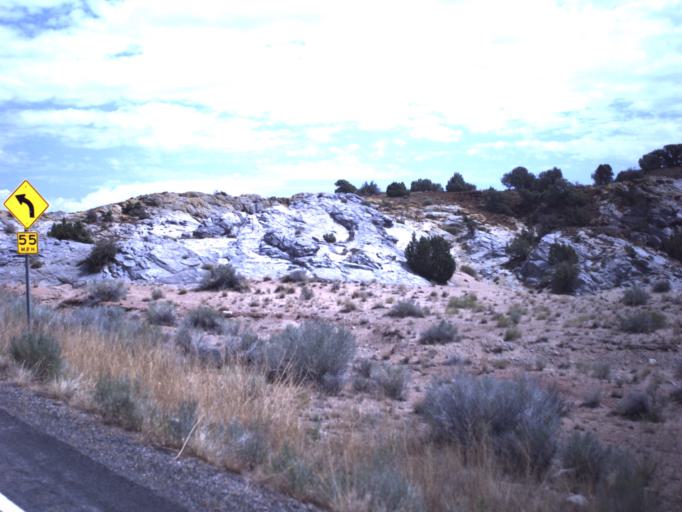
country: US
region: Utah
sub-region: Uintah County
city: Naples
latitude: 40.3401
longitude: -109.4842
